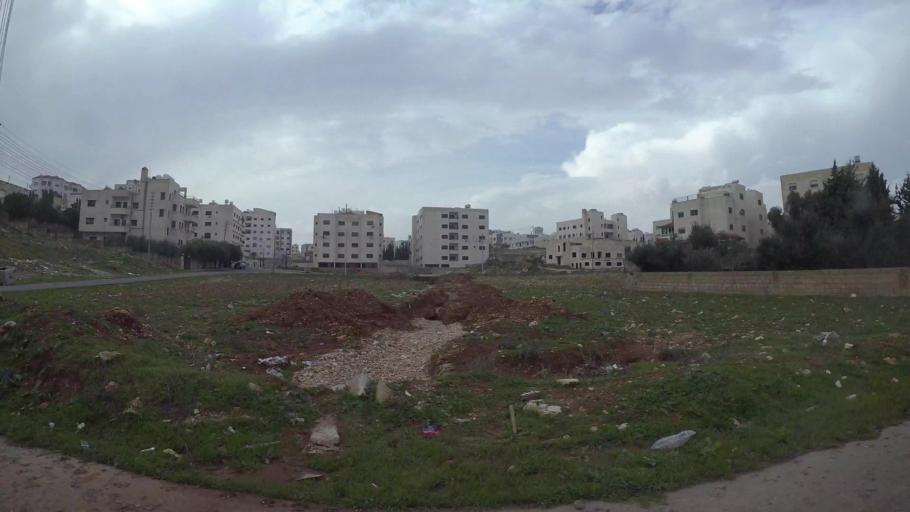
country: JO
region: Amman
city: Umm as Summaq
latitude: 31.8822
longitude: 35.8670
